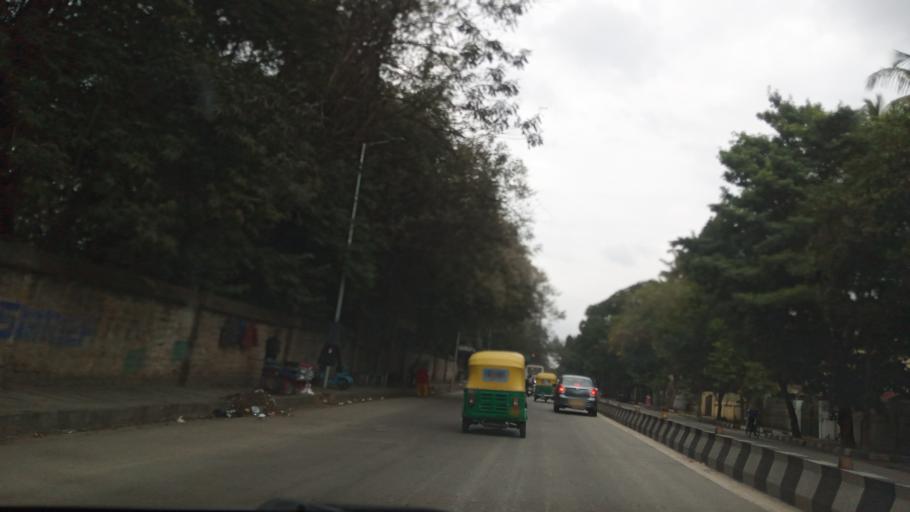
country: IN
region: Karnataka
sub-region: Bangalore Urban
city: Bangalore
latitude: 13.0001
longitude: 77.5949
